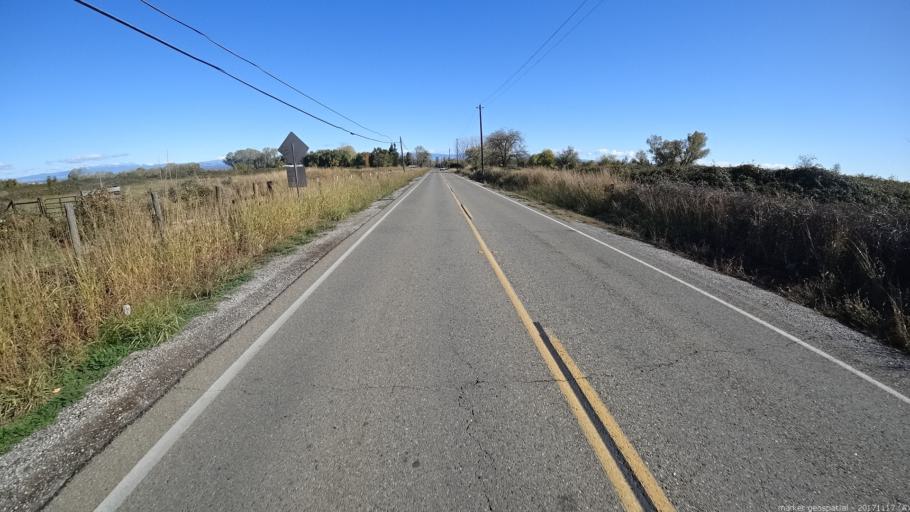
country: US
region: California
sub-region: Shasta County
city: Cottonwood
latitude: 40.4040
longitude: -122.2422
